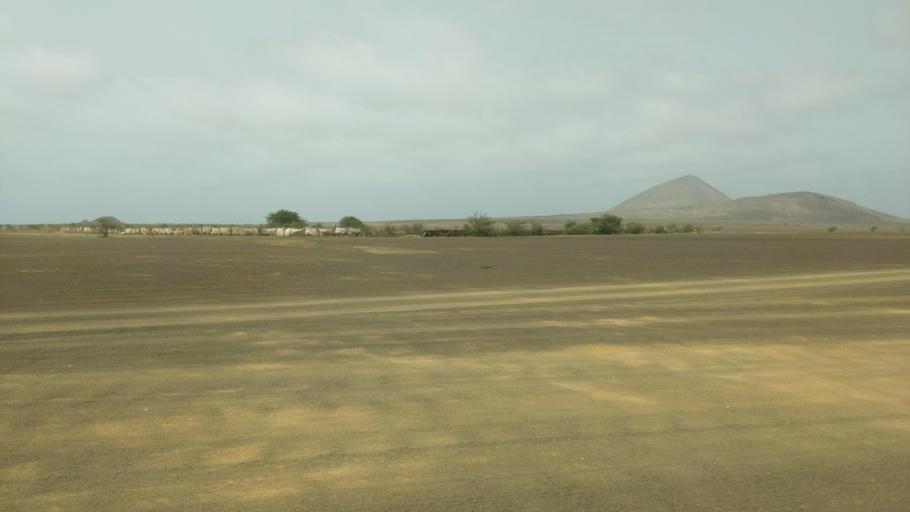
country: CV
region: Sal
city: Espargos
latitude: 16.7963
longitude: -22.9543
